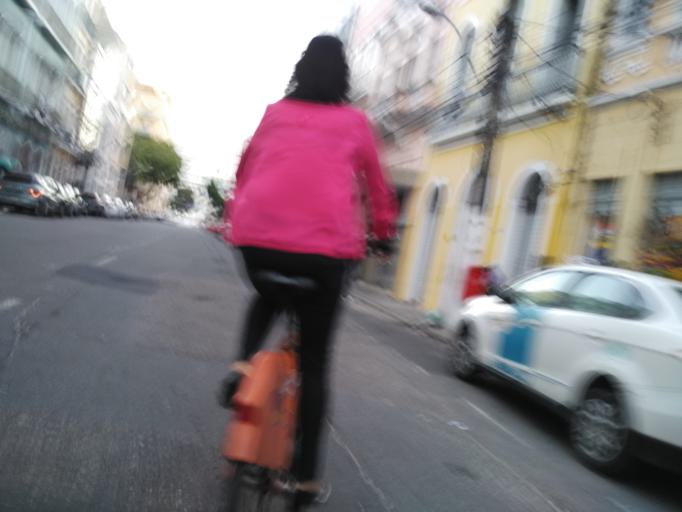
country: BR
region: Pernambuco
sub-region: Recife
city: Recife
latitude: -8.0643
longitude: -34.8768
